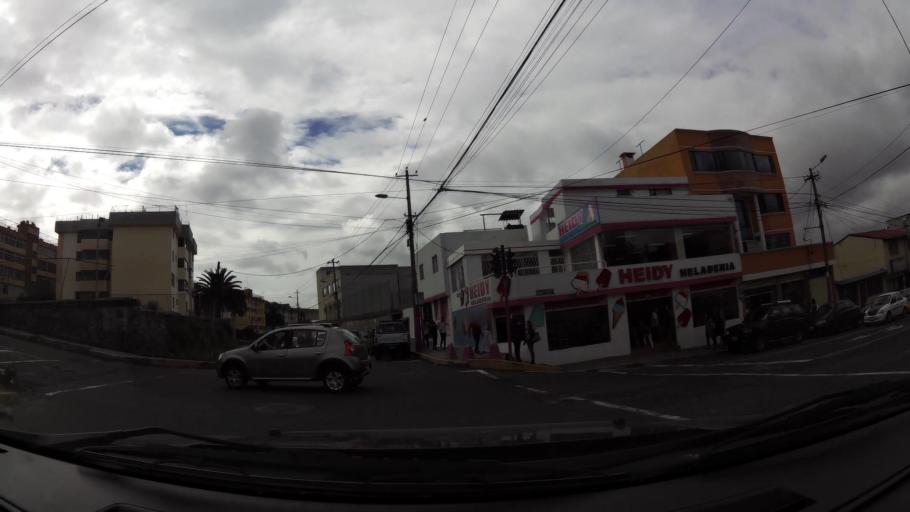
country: EC
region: Pichincha
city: Quito
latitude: -0.1292
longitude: -78.5015
